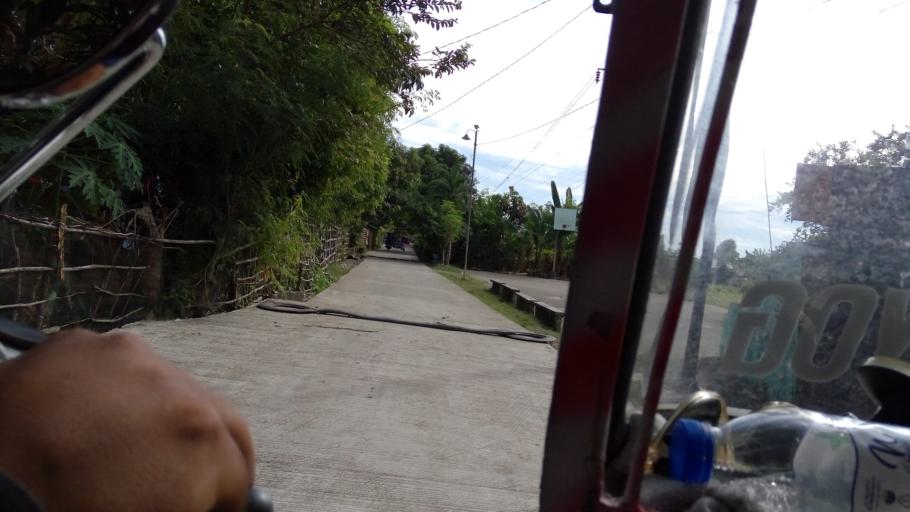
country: PH
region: Ilocos
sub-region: Province of La Union
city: San Eugenio
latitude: 16.3613
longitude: 120.3526
